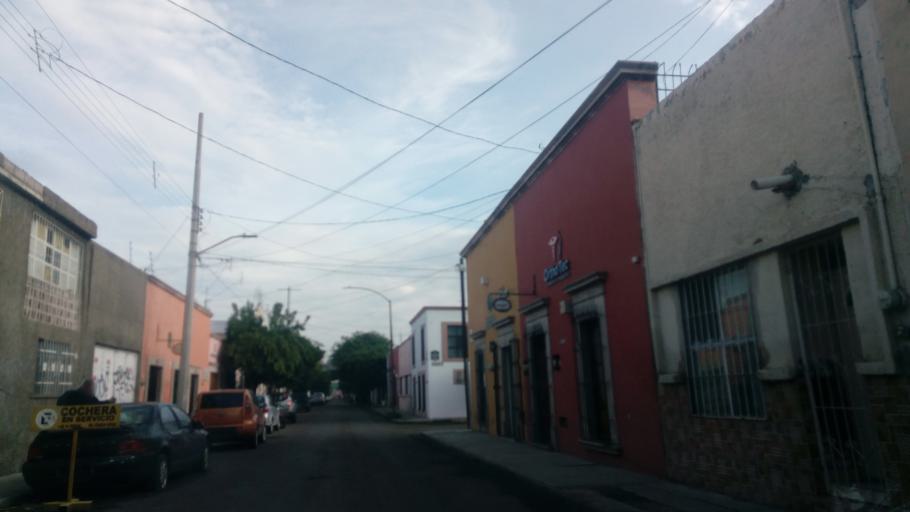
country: MX
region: Durango
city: Victoria de Durango
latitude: 24.0318
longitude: -104.6706
